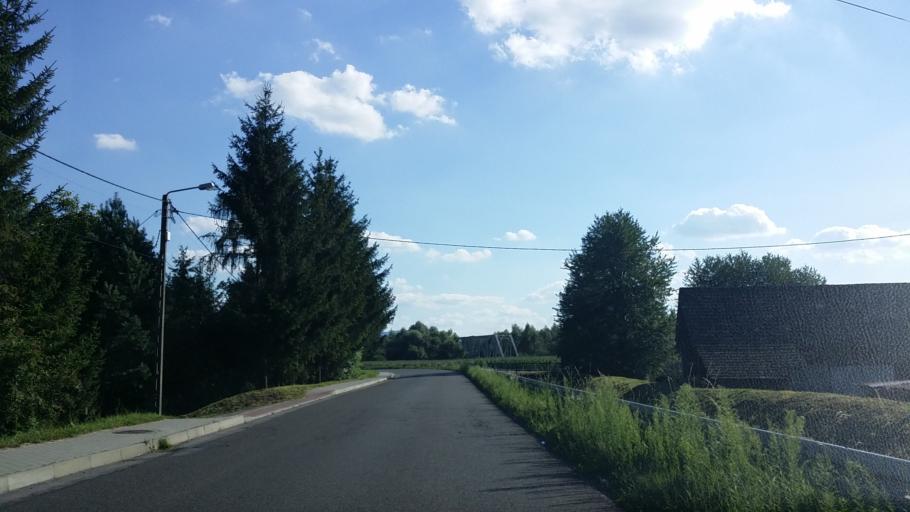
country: PL
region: Lesser Poland Voivodeship
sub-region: Powiat wadowicki
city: Wozniki
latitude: 49.9343
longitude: 19.4861
